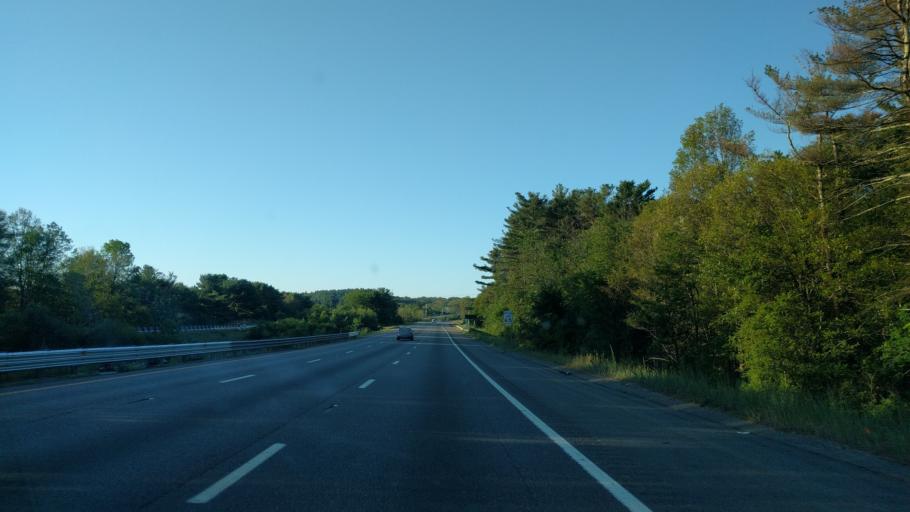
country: US
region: Massachusetts
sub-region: Middlesex County
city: Marlborough
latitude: 42.3123
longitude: -71.5678
